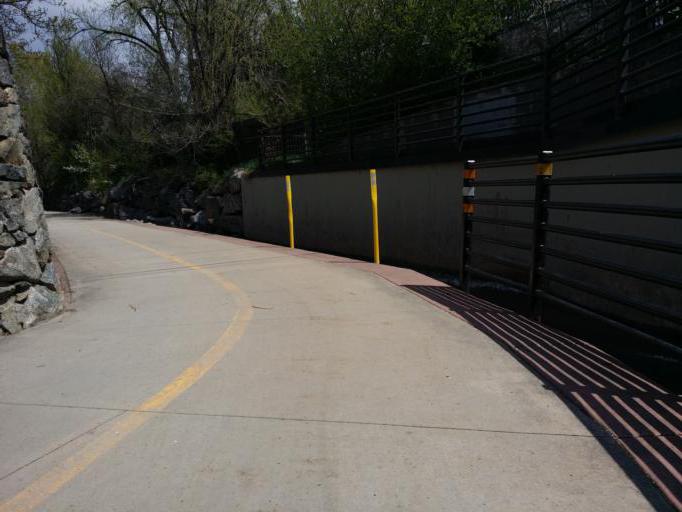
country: US
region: Colorado
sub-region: Boulder County
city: Boulder
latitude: 39.9919
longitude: -105.2498
